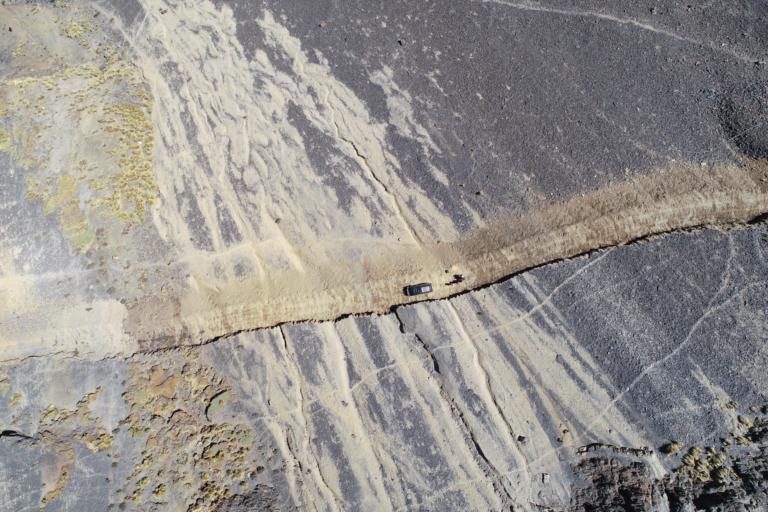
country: BO
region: La Paz
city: La Paz
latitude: -16.6218
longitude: -67.8229
